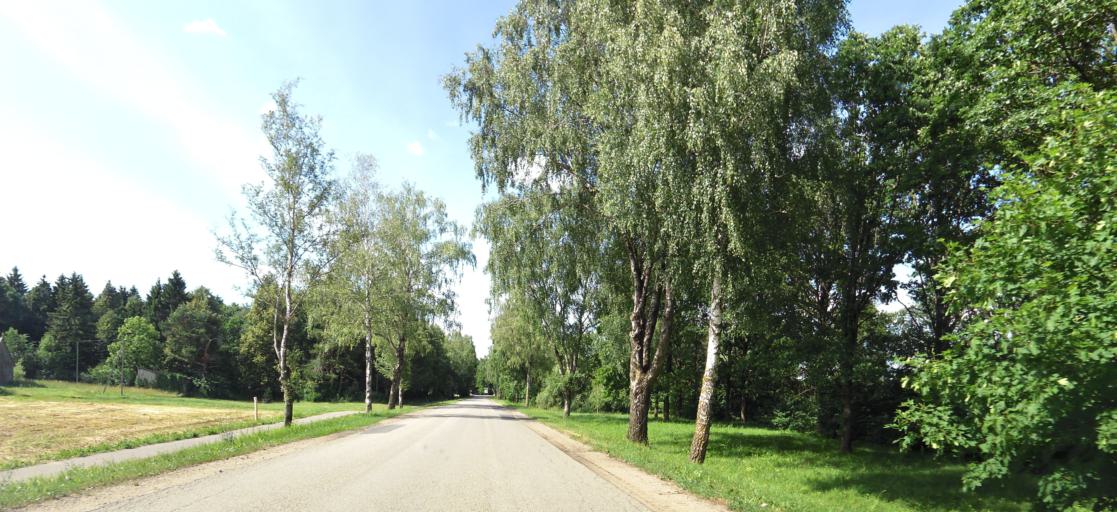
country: LT
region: Panevezys
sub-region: Birzai
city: Birzai
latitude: 56.1948
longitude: 24.6282
